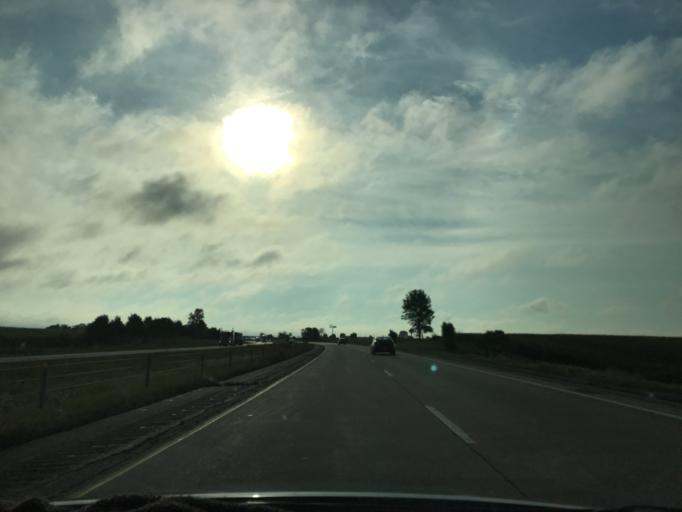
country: US
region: Iowa
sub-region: Cedar County
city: West Branch
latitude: 41.6645
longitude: -91.3592
